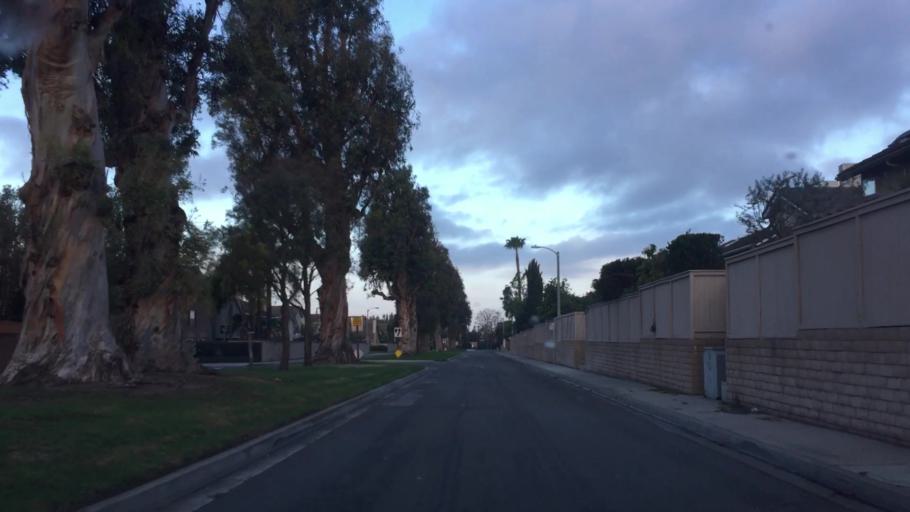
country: US
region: California
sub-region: Orange County
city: North Tustin
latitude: 33.7076
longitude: -117.7746
